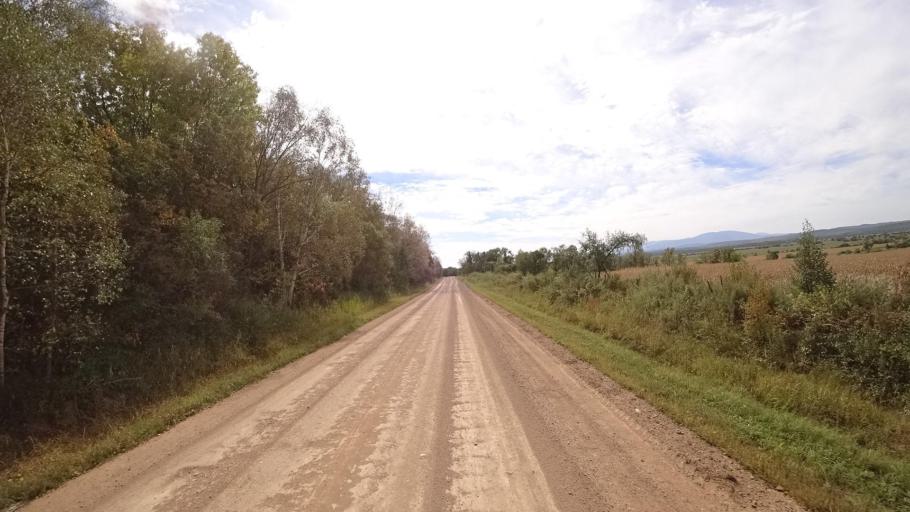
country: RU
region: Primorskiy
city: Yakovlevka
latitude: 44.5760
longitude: 133.5949
